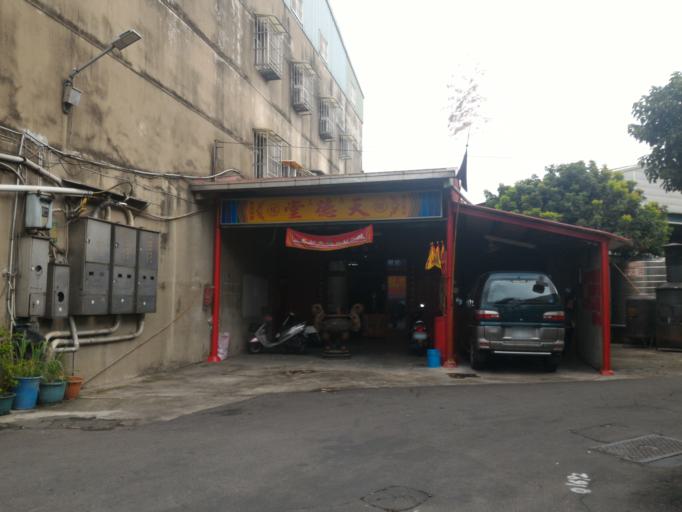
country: TW
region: Taiwan
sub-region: Taoyuan
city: Taoyuan
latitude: 24.9586
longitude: 121.3904
